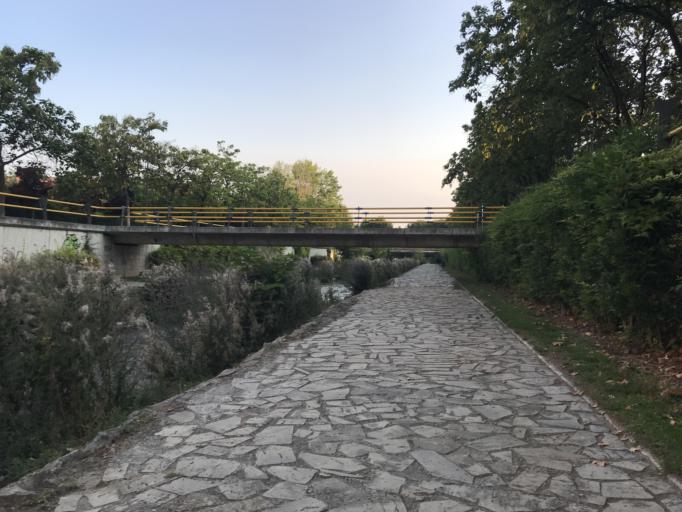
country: ES
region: Castille and Leon
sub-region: Provincia de Valladolid
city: Valladolid
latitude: 41.6553
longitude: -4.7113
